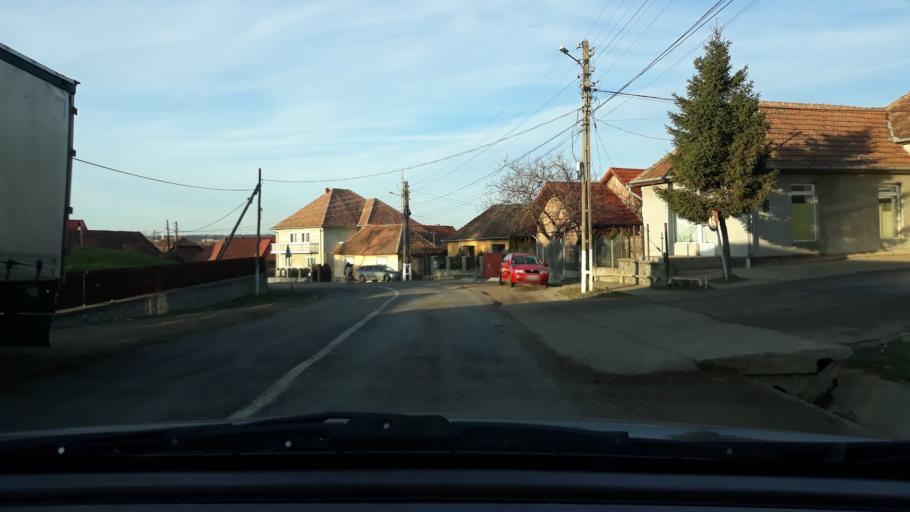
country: RO
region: Bihor
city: Foglas
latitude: 47.2522
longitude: 22.5328
